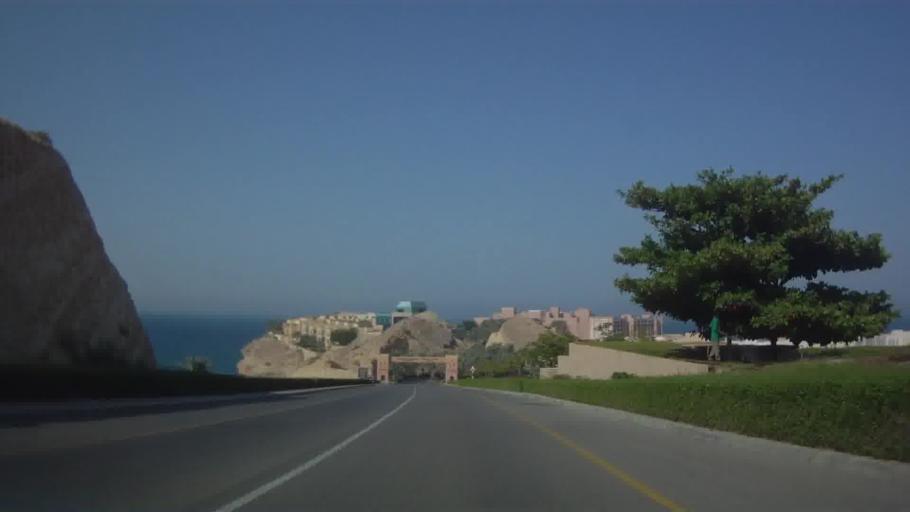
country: OM
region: Muhafazat Masqat
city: Muscat
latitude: 23.5476
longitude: 58.6571
